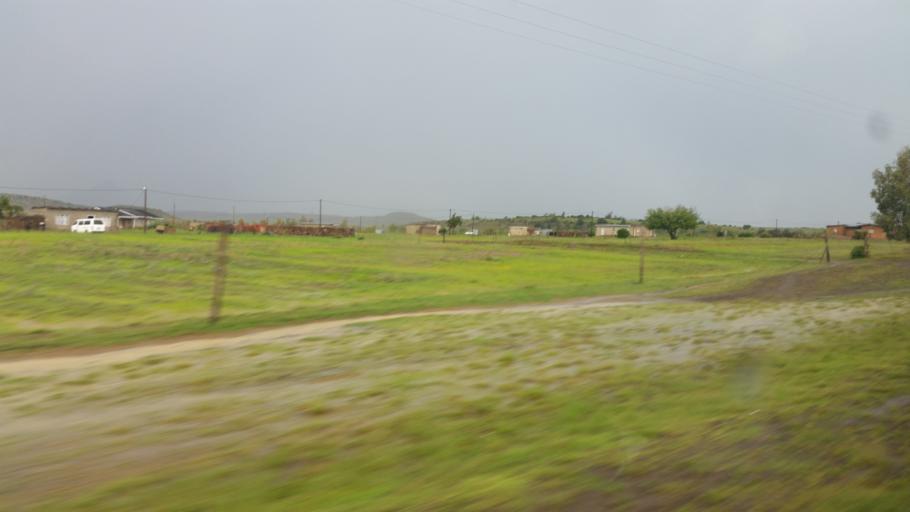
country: LS
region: Mafeteng
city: Mafeteng
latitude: -29.7528
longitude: 27.1603
